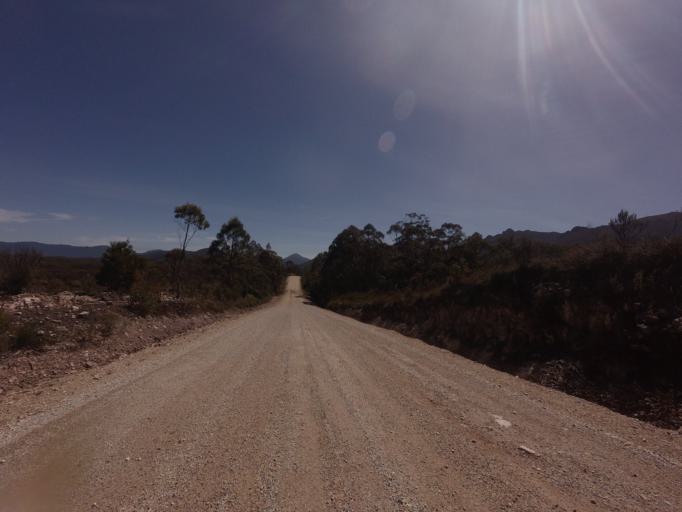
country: AU
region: Tasmania
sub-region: Huon Valley
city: Geeveston
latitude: -42.9667
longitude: 146.3617
